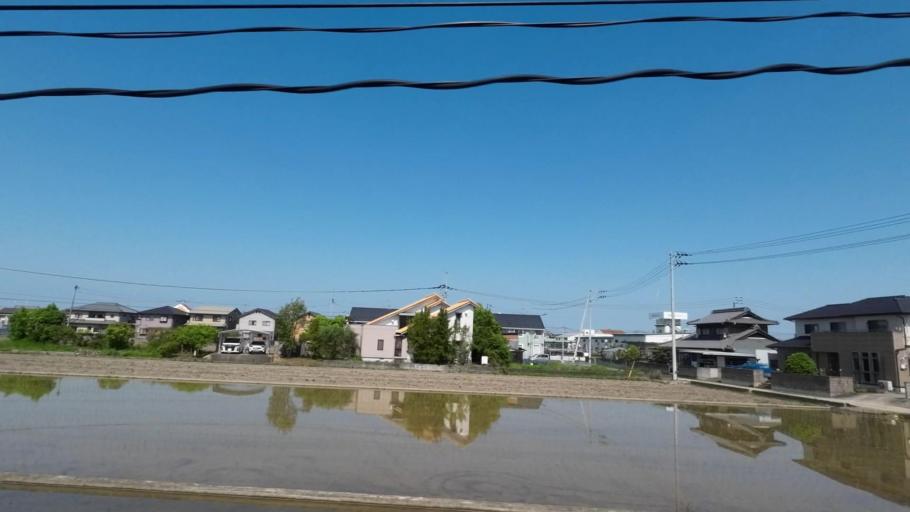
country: JP
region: Kagawa
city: Kan'onjicho
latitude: 34.1206
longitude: 133.6479
